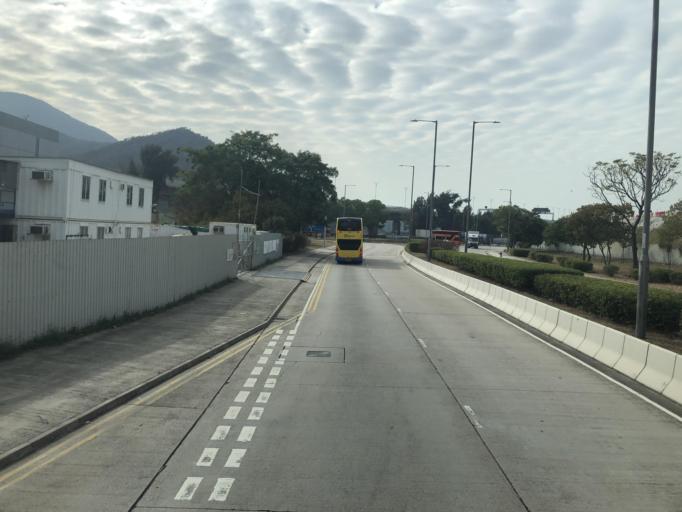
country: HK
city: Tai O
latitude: 22.2947
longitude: 113.9233
